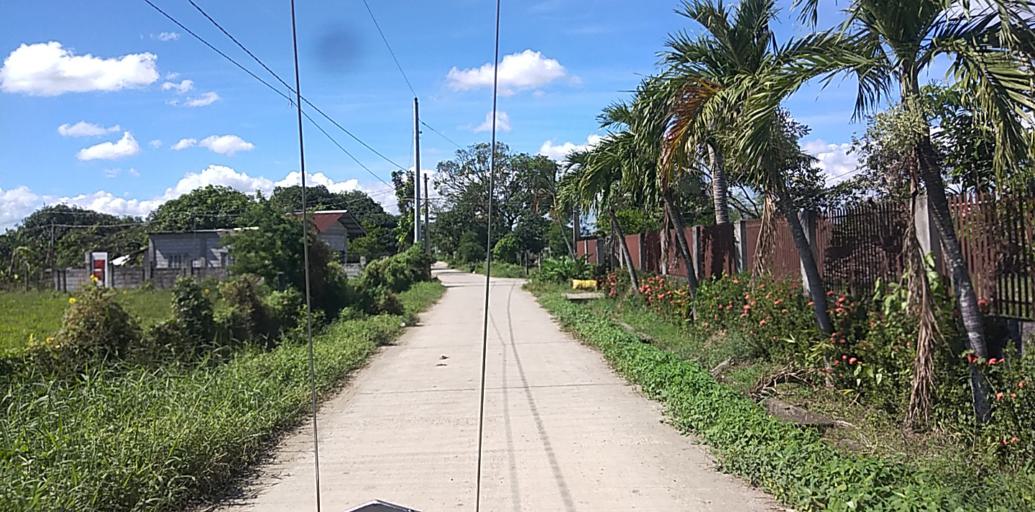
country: PH
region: Central Luzon
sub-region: Province of Pampanga
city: Arayat
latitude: 15.1276
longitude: 120.7848
